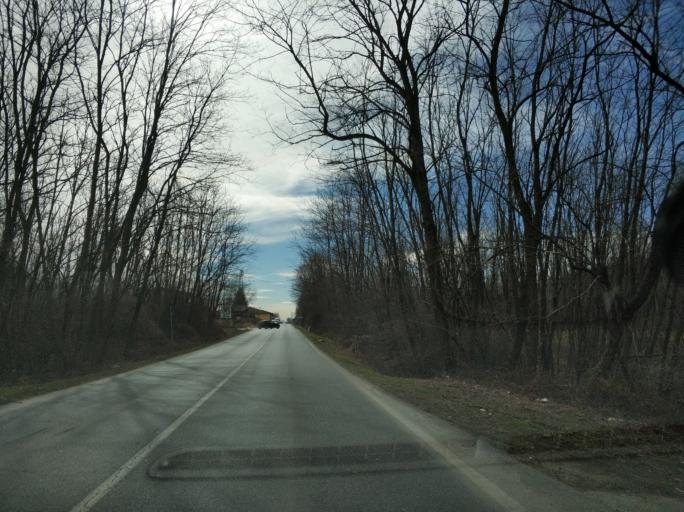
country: IT
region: Piedmont
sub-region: Provincia di Torino
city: Lombardore
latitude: 45.2186
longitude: 7.7307
